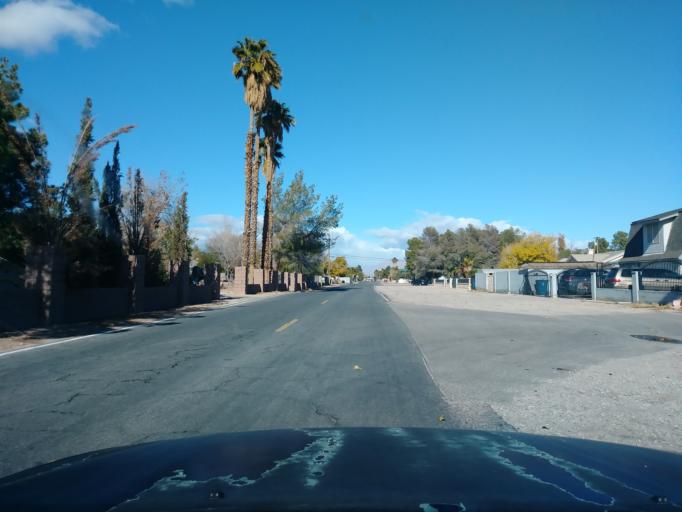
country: US
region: Nevada
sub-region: Clark County
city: Spring Valley
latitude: 36.1488
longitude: -115.2190
